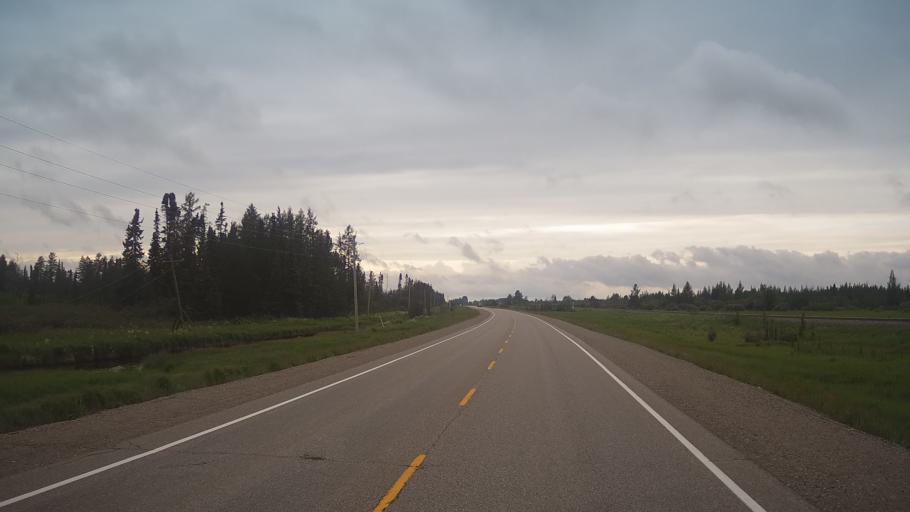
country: CA
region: Ontario
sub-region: Thunder Bay District
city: Thunder Bay
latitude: 48.8736
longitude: -89.9794
